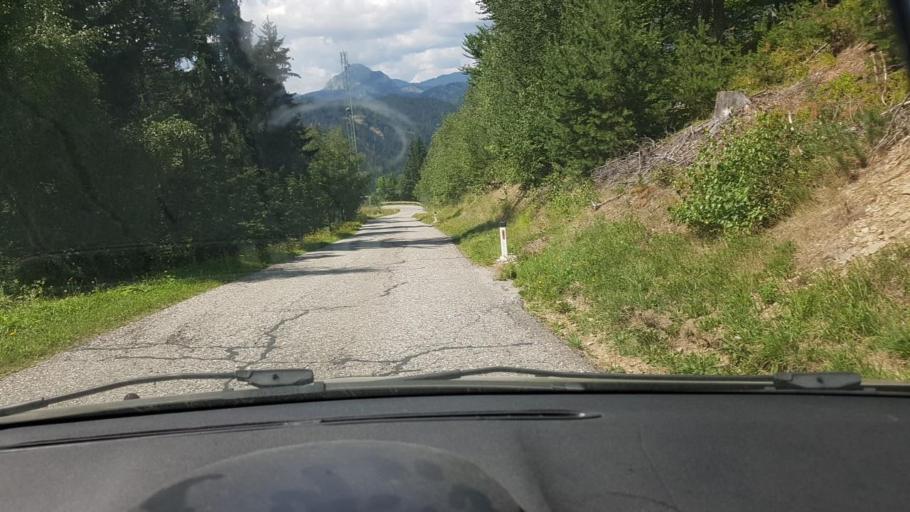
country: SI
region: Jezersko
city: Zgornje Jezersko
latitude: 46.4172
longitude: 14.5660
